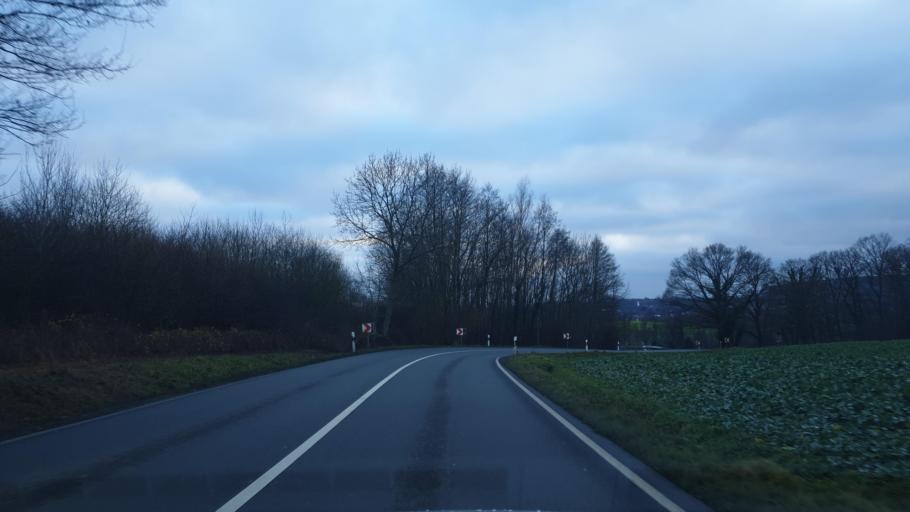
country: DE
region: North Rhine-Westphalia
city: Loehne
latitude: 52.1714
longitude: 8.6845
